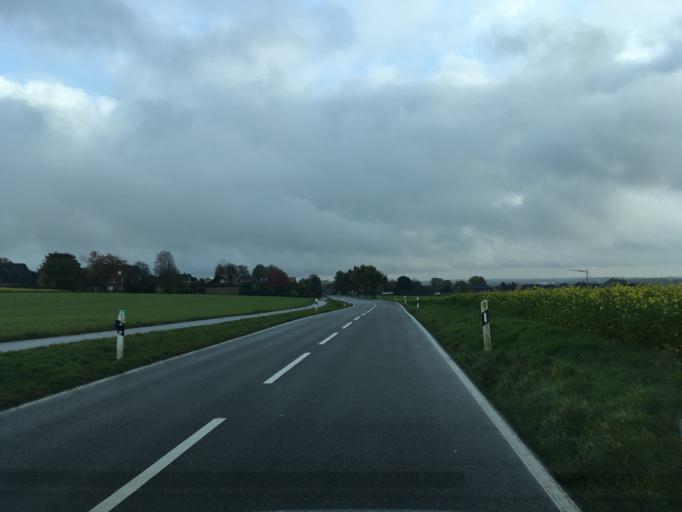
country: DE
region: North Rhine-Westphalia
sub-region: Regierungsbezirk Munster
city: Klein Reken
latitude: 51.8374
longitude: 7.0338
